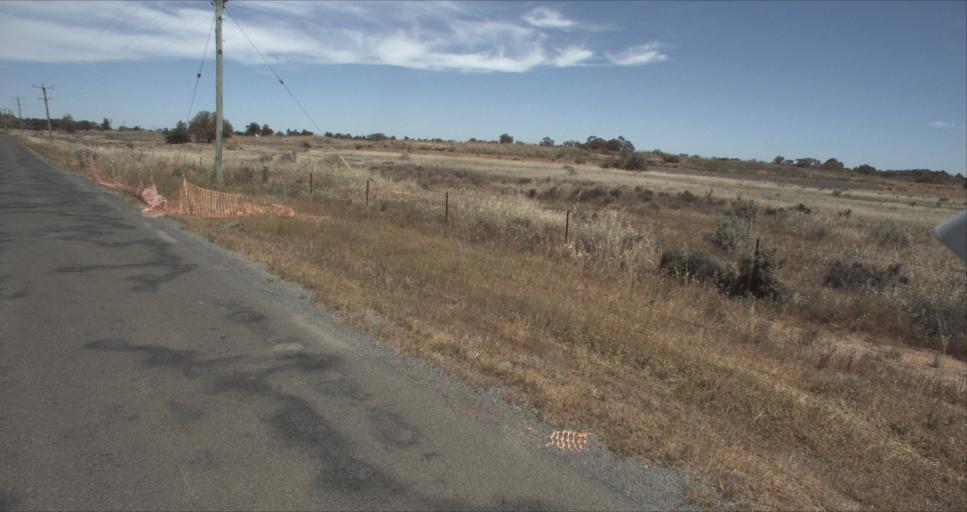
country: AU
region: New South Wales
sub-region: Leeton
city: Leeton
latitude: -34.6059
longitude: 146.4261
